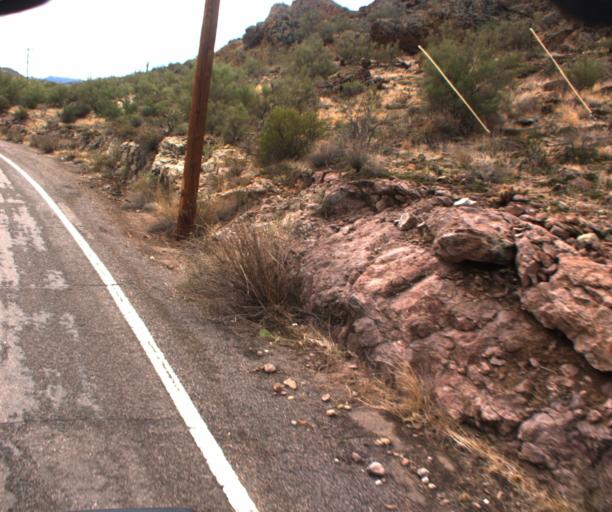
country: US
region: Arizona
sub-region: Pinal County
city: Apache Junction
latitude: 33.5176
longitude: -111.4582
